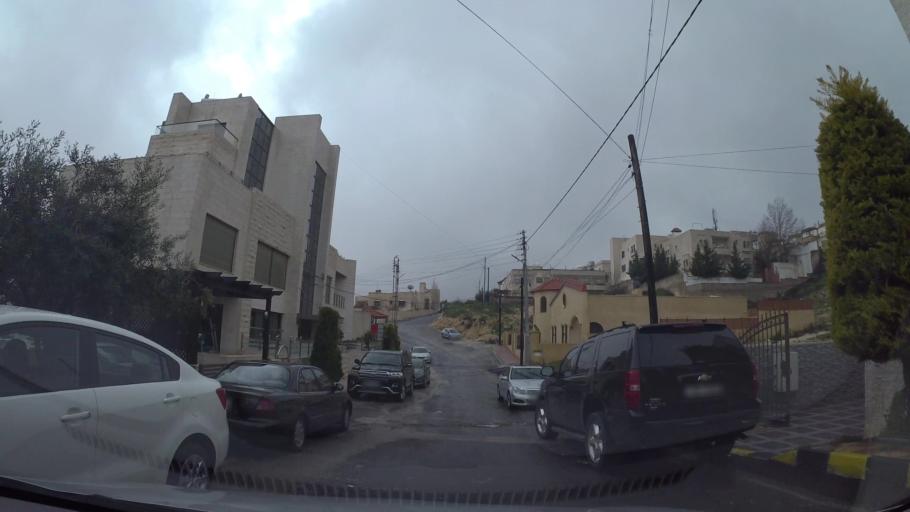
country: JO
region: Amman
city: Al Jubayhah
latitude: 32.0158
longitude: 35.8307
